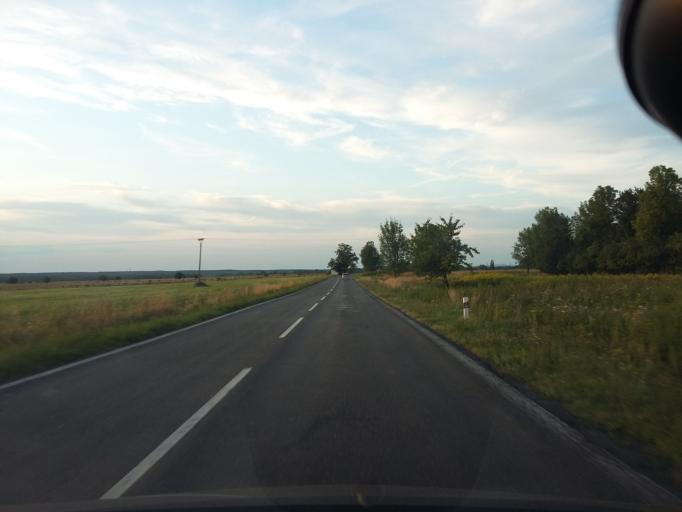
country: SK
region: Bratislavsky
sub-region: Okres Malacky
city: Malacky
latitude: 48.4089
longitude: 17.1563
